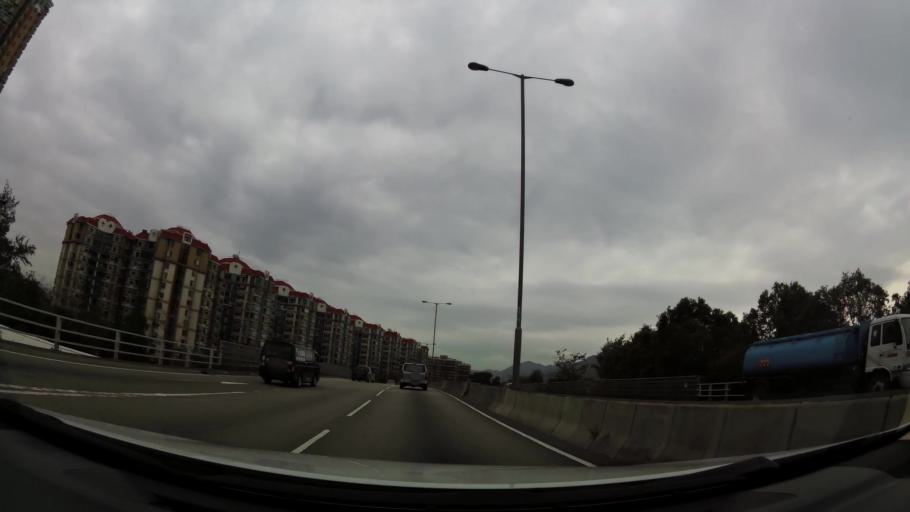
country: HK
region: Yuen Long
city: Yuen Long Kau Hui
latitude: 22.4445
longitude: 114.0167
